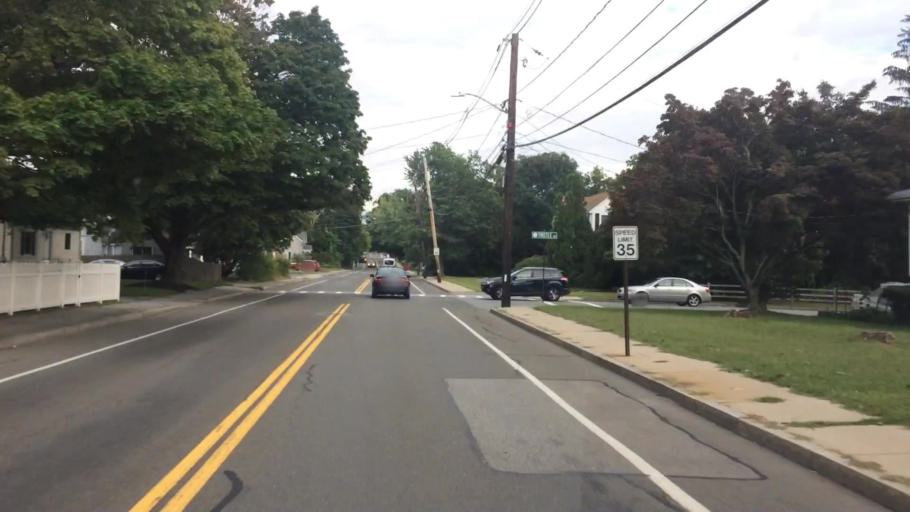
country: US
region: Massachusetts
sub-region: Middlesex County
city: Woburn
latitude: 42.4886
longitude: -71.1692
